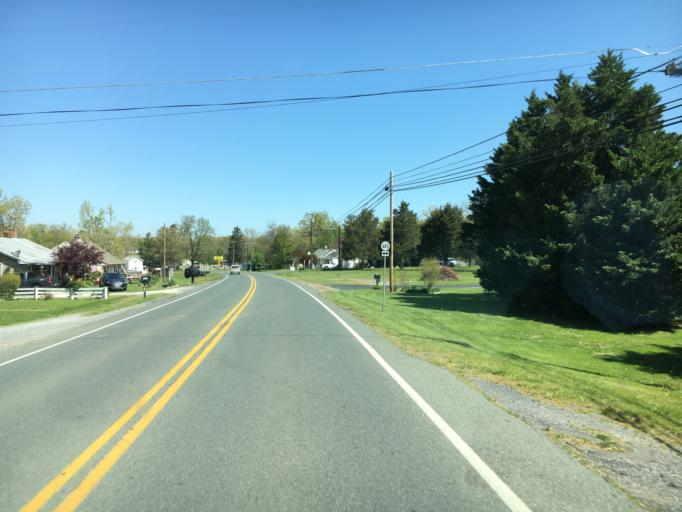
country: US
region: Virginia
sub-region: Augusta County
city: Crimora
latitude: 38.1483
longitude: -78.8407
